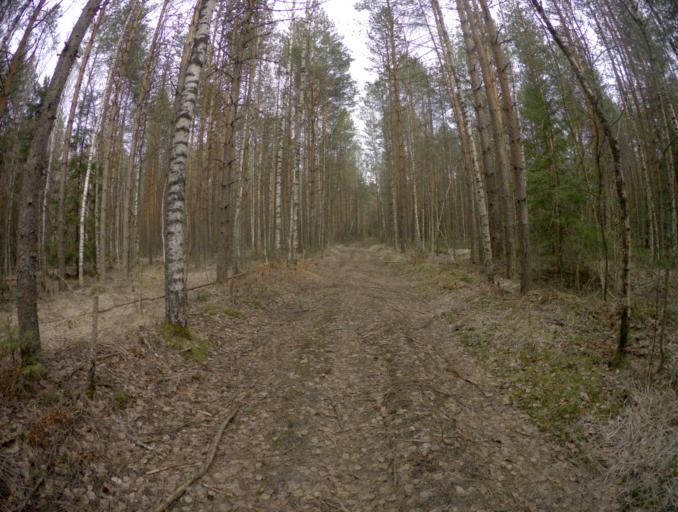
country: RU
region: Vladimir
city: Raduzhnyy
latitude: 55.9321
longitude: 40.2745
